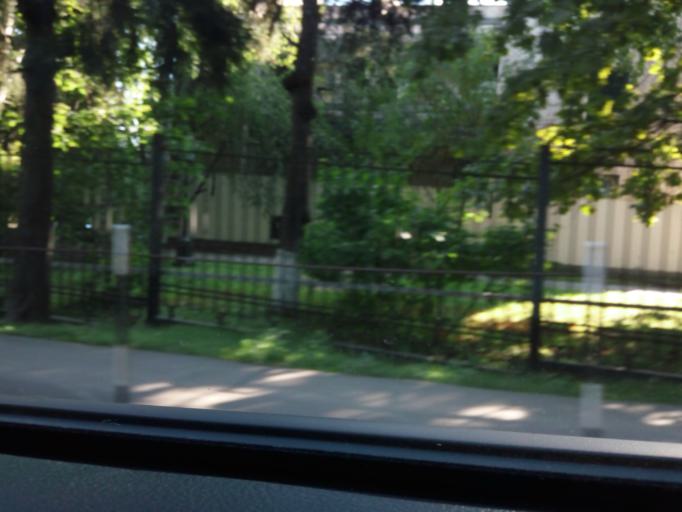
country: RU
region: Moskovskaya
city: Levoberezhnaya
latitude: 55.8807
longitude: 37.4647
